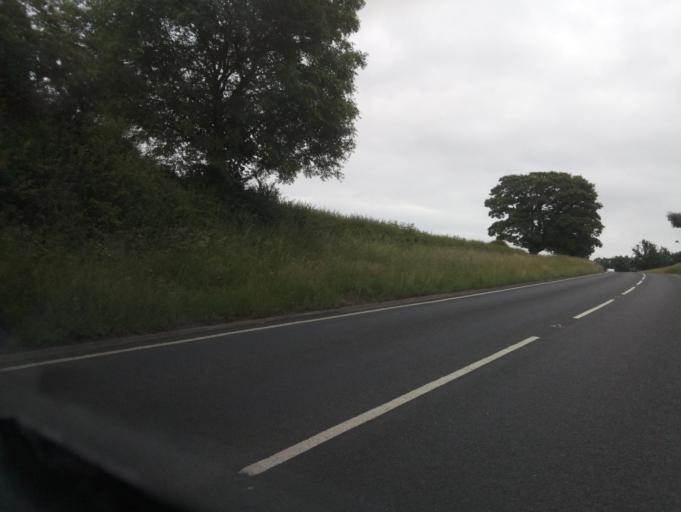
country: GB
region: England
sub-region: District of Rutland
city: Empingham
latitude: 52.6615
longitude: -0.5929
